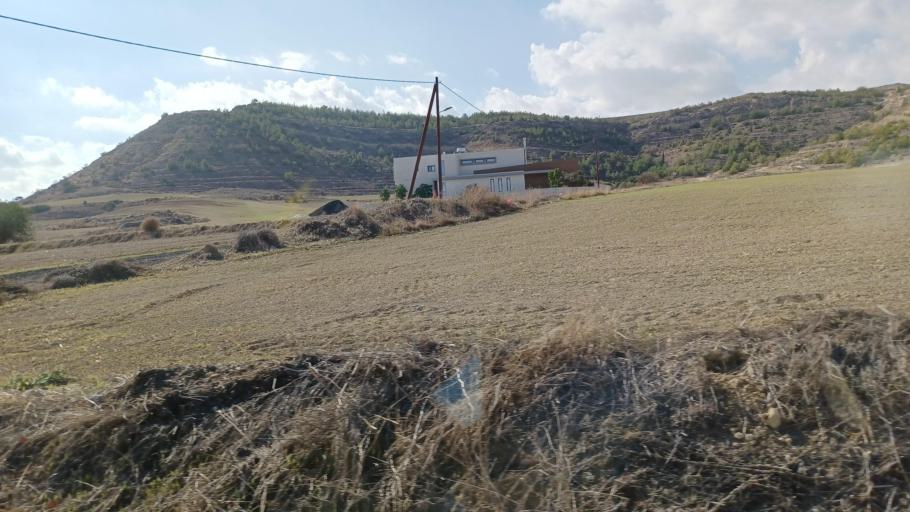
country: CY
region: Larnaka
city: Voroklini
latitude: 34.9962
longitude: 33.6548
